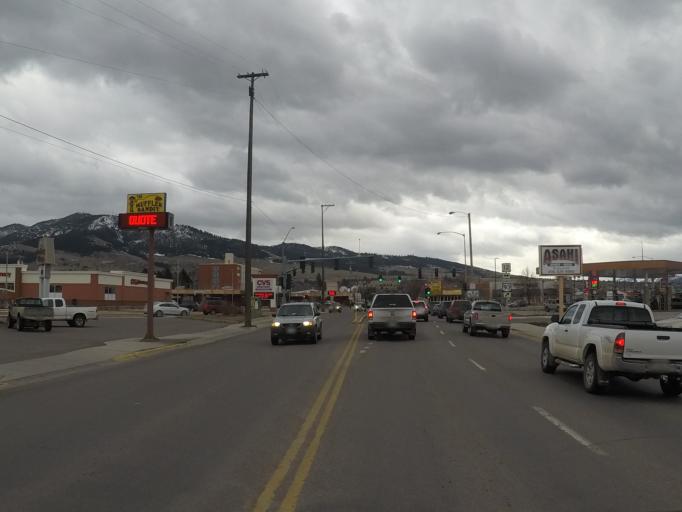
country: US
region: Montana
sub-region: Missoula County
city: Missoula
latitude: 46.8529
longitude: -114.0131
